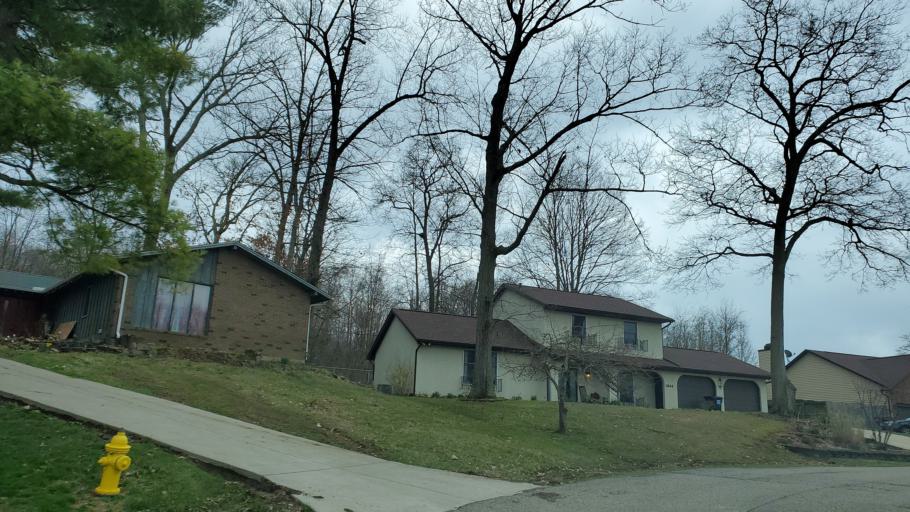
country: US
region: Ohio
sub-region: Licking County
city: Newark
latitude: 40.0230
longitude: -82.3779
